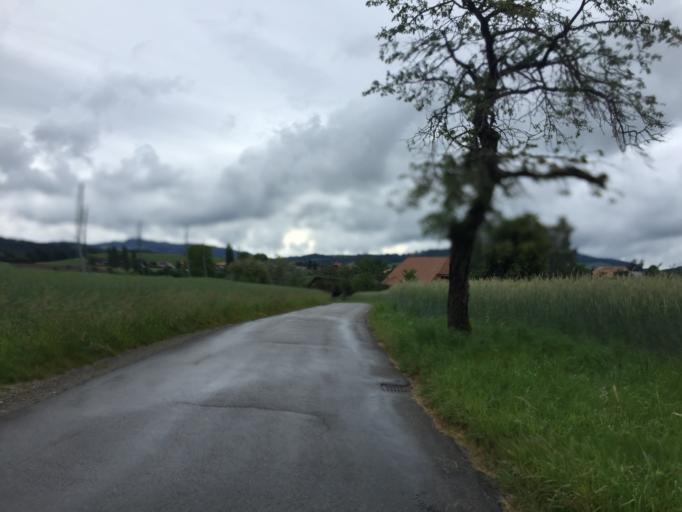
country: CH
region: Bern
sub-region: Bern-Mittelland District
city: Taegertschi
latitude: 46.8974
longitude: 7.5773
